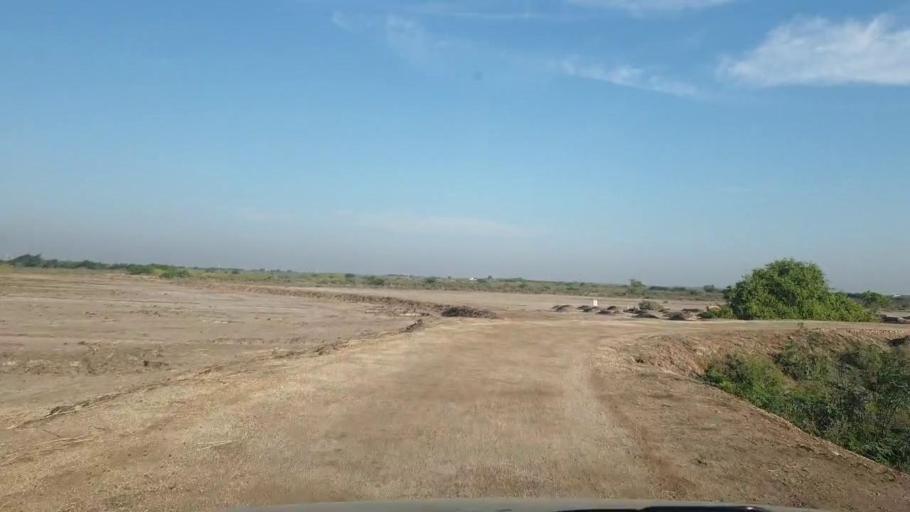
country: PK
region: Sindh
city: Talhar
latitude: 24.8325
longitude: 68.8386
